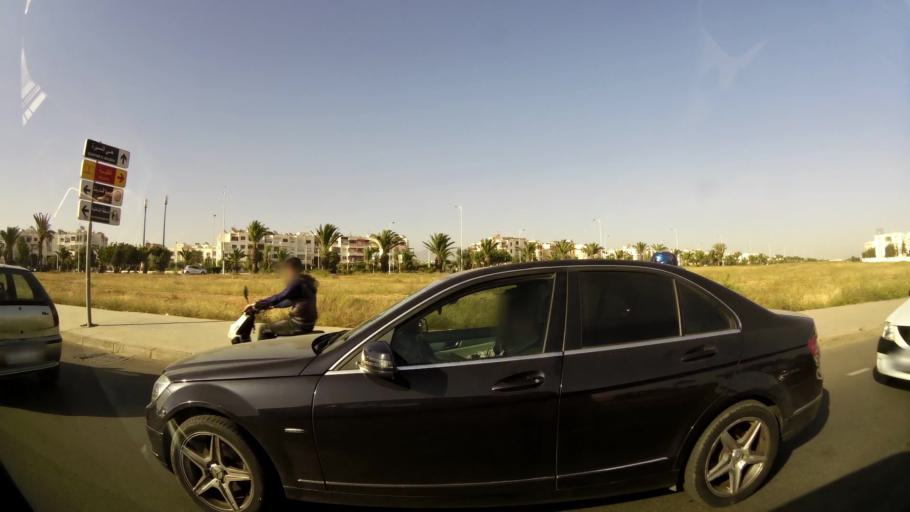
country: MA
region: Oued ed Dahab-Lagouira
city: Dakhla
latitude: 30.4031
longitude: -9.5583
